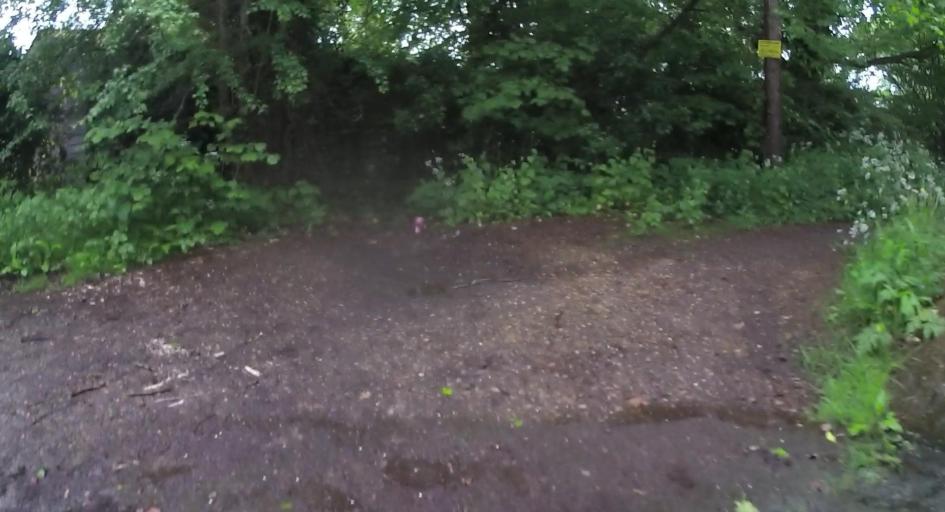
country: GB
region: England
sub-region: Wokingham
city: Wokingham
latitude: 51.3940
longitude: -0.8114
